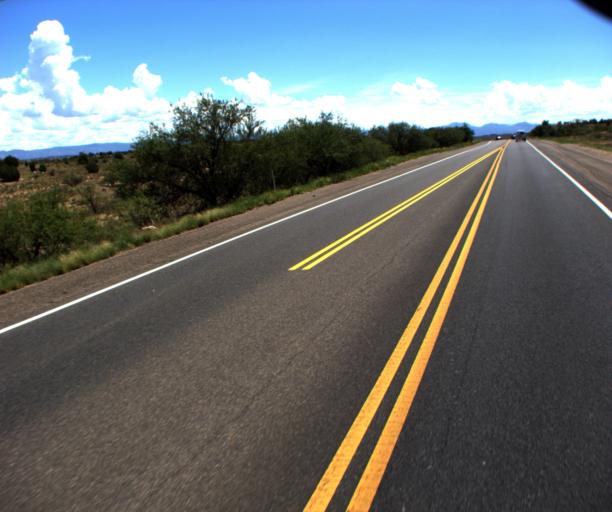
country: US
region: Arizona
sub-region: Yavapai County
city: Cornville
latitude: 34.6509
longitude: -111.9570
